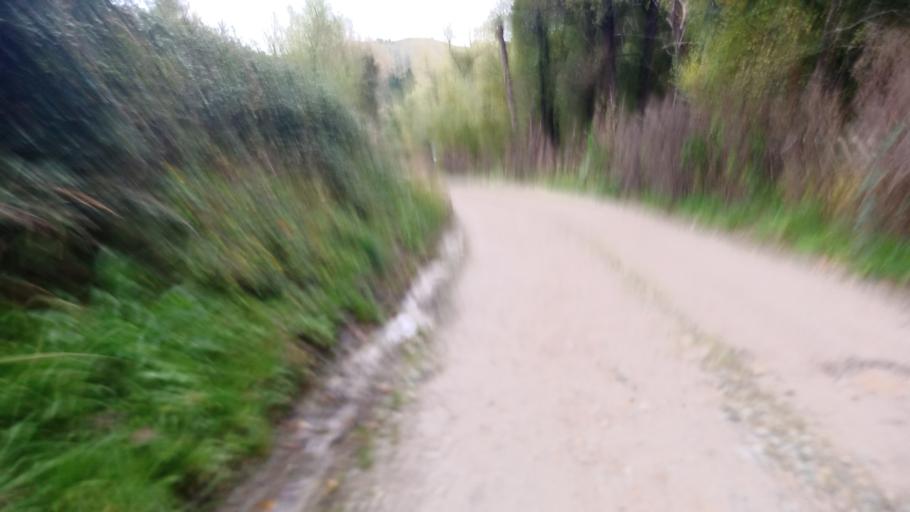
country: NZ
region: Gisborne
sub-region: Gisborne District
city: Gisborne
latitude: -38.6475
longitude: 178.0437
